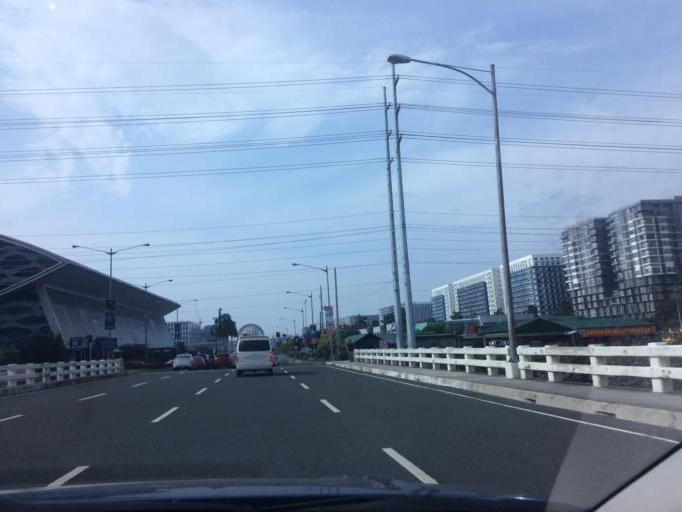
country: PH
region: Metro Manila
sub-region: Makati City
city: Makati City
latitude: 14.5302
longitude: 120.9848
